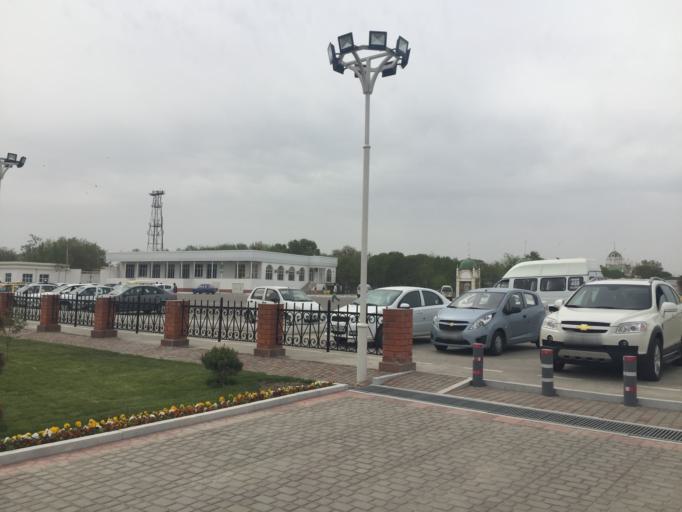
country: UZ
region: Bukhara
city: Kogon
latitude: 39.7230
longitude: 64.5477
